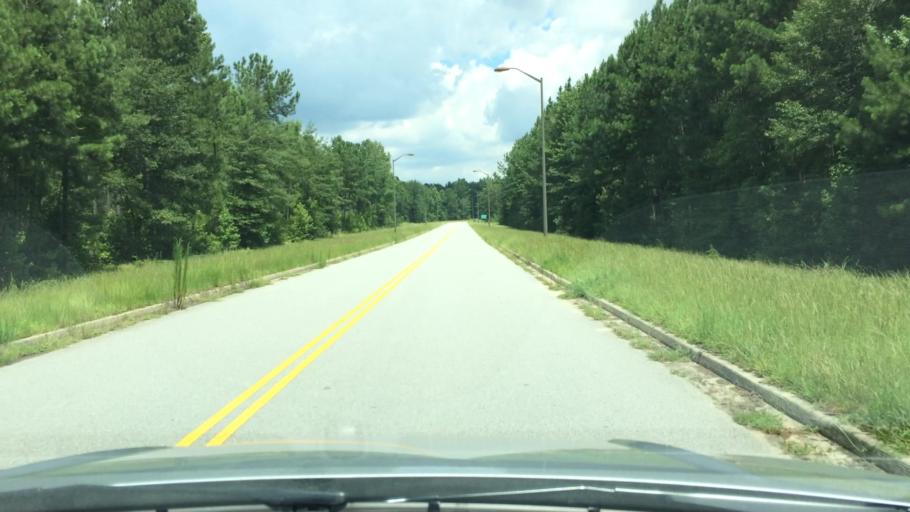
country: US
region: South Carolina
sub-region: Calhoun County
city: Oak Grove
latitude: 33.7982
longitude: -81.0037
